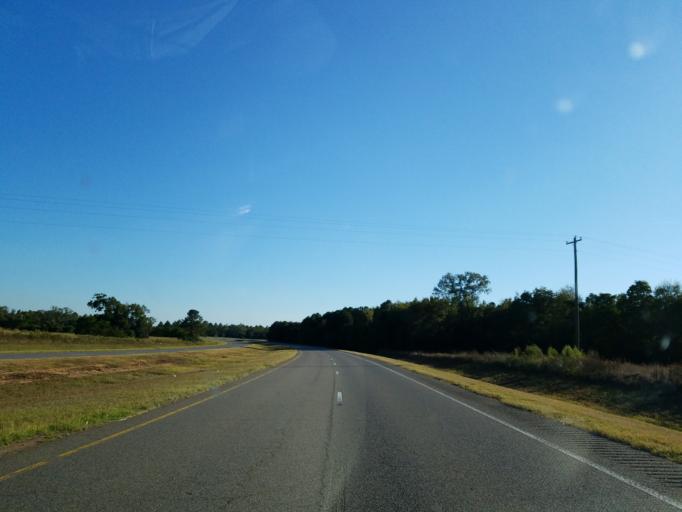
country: US
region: Georgia
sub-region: Lee County
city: Leesburg
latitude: 31.7328
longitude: -84.1822
